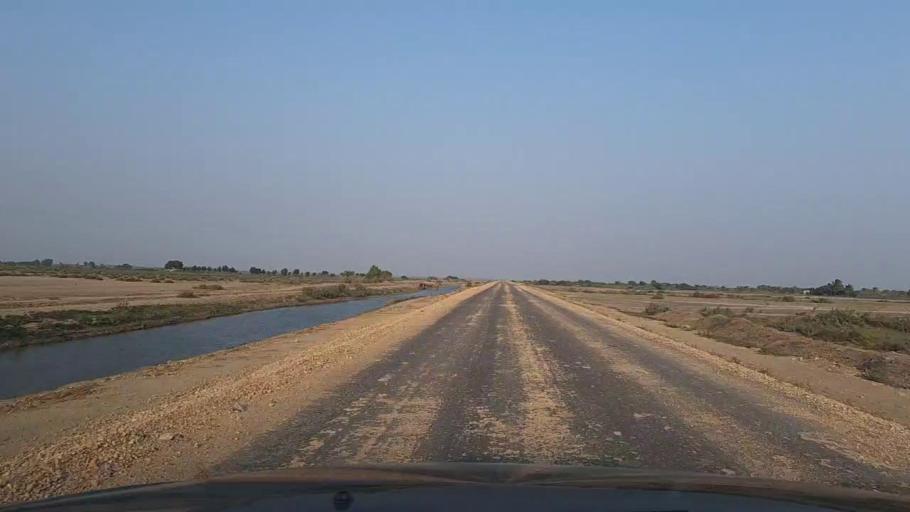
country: PK
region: Sindh
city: Mirpur Sakro
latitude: 24.4207
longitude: 67.7429
